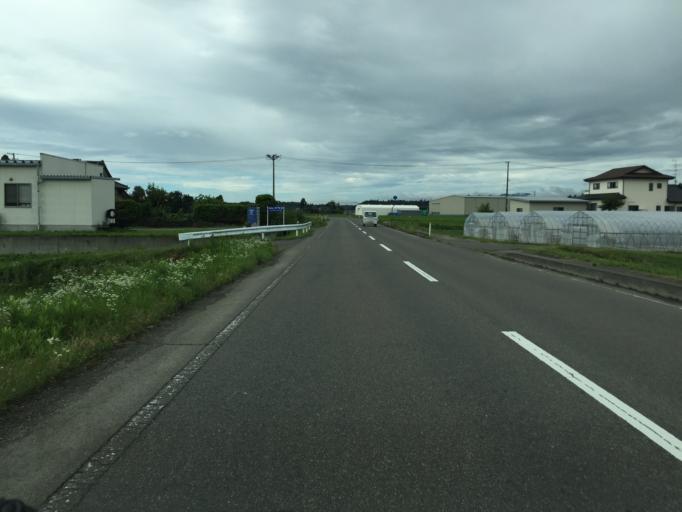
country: JP
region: Miyagi
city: Marumori
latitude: 37.7694
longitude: 140.9500
